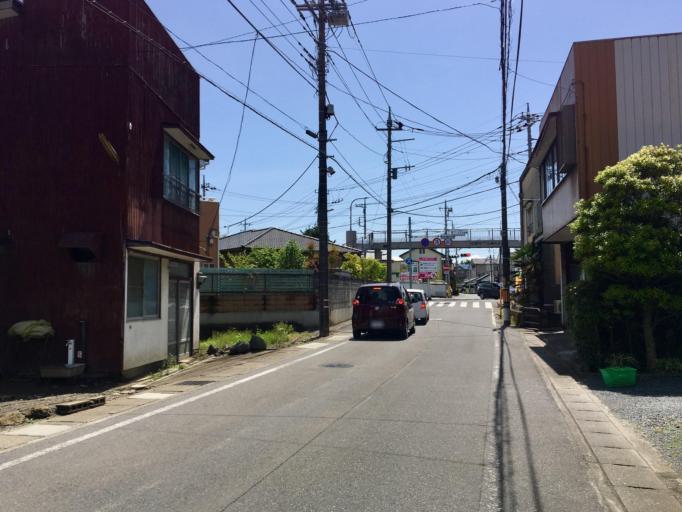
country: JP
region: Tochigi
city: Sano
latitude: 36.3143
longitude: 139.5679
